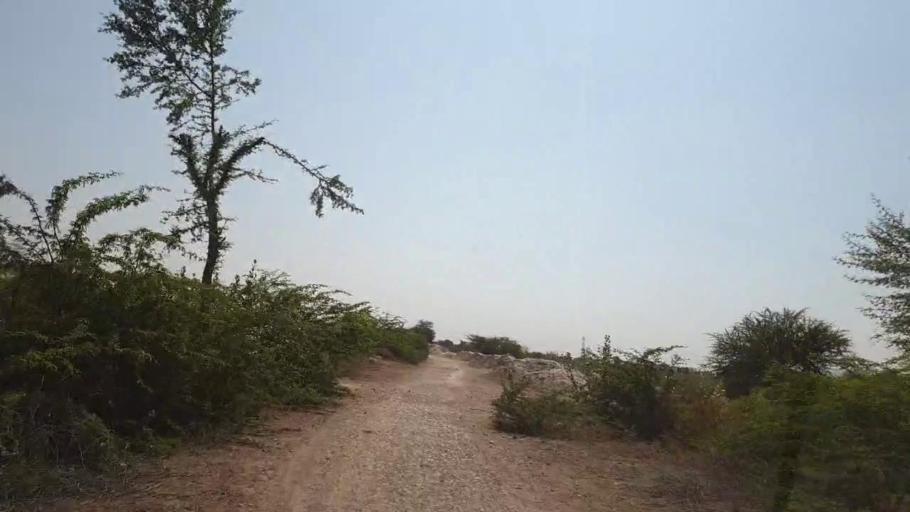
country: PK
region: Sindh
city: Nabisar
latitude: 25.0761
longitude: 69.5339
